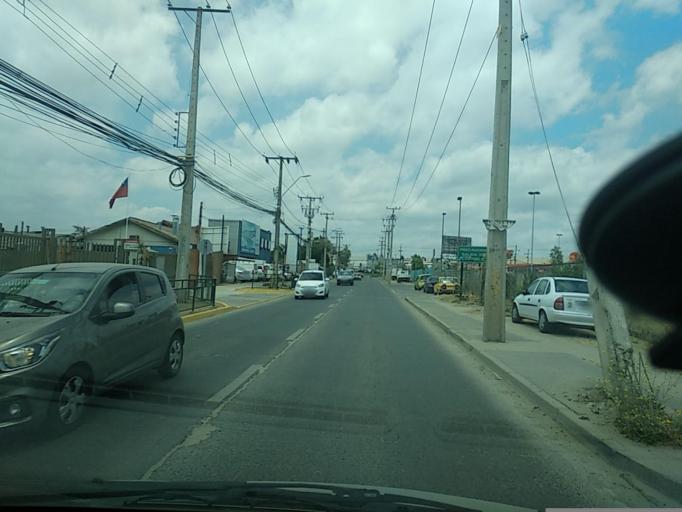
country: CL
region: Valparaiso
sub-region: Provincia de Marga Marga
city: Quilpue
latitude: -33.0424
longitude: -71.4195
